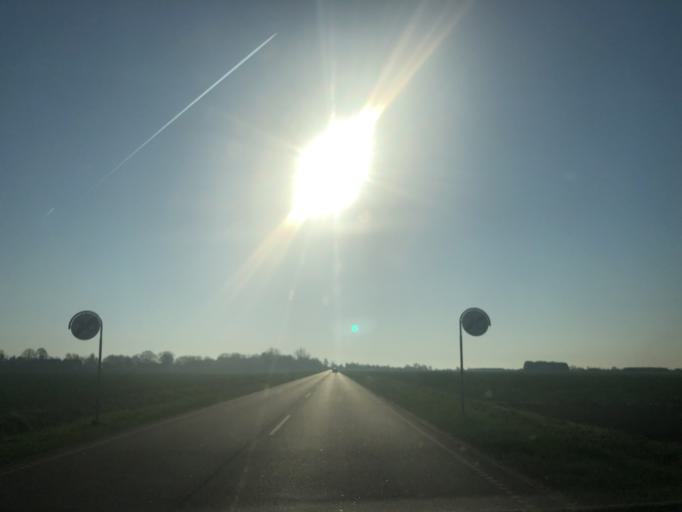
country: DK
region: Zealand
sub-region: Faxe Kommune
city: Haslev
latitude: 55.3590
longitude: 11.9052
